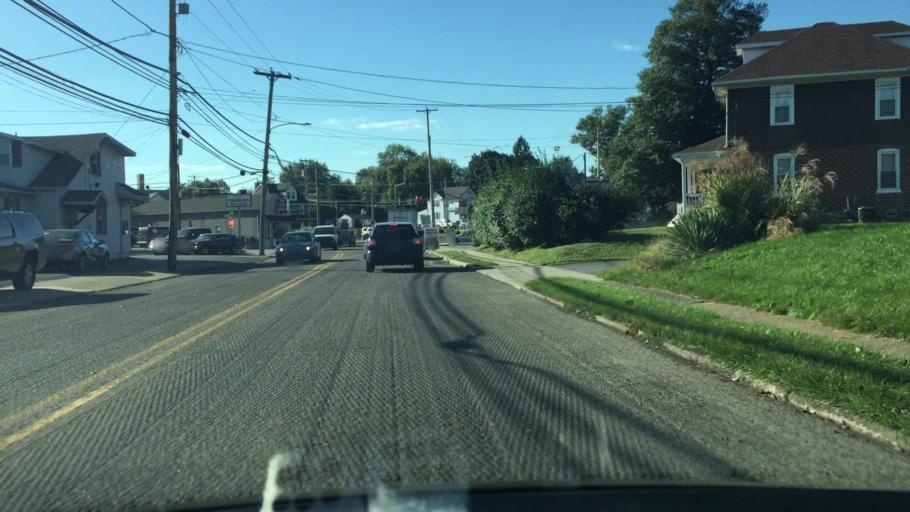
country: US
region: Pennsylvania
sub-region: Delaware County
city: Boothwyn
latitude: 39.8303
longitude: -75.4380
